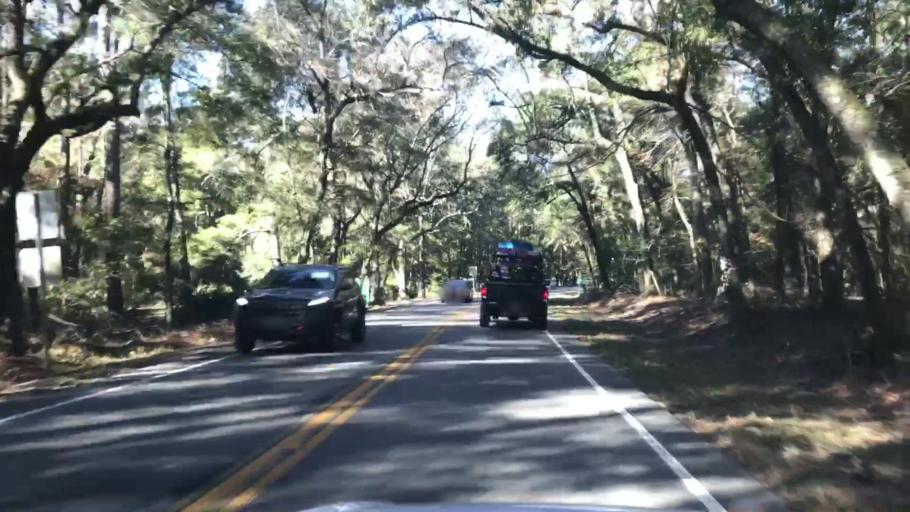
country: US
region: South Carolina
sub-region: Berkeley County
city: Ladson
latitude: 32.8900
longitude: -80.1269
